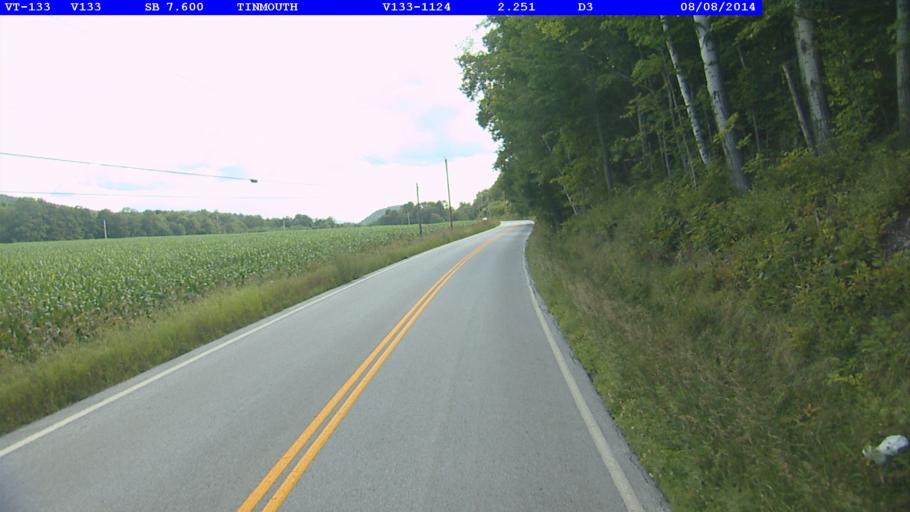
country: US
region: Vermont
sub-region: Rutland County
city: Poultney
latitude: 43.4339
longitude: -73.1121
